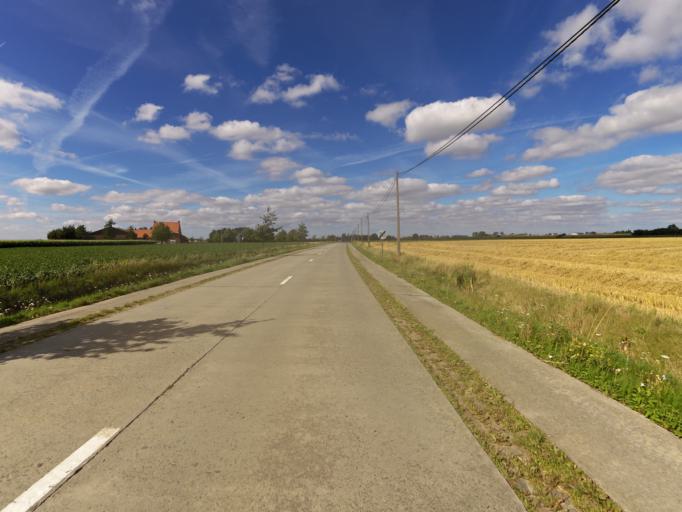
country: FR
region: Nord-Pas-de-Calais
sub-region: Departement du Nord
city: Steenvoorde
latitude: 50.8663
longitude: 2.6211
